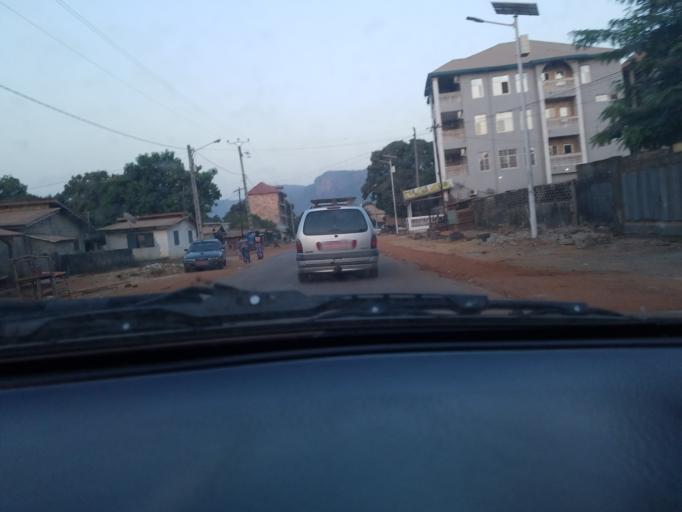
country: GN
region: Kindia
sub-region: Prefecture de Dubreka
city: Dubreka
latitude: 9.7884
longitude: -13.5082
